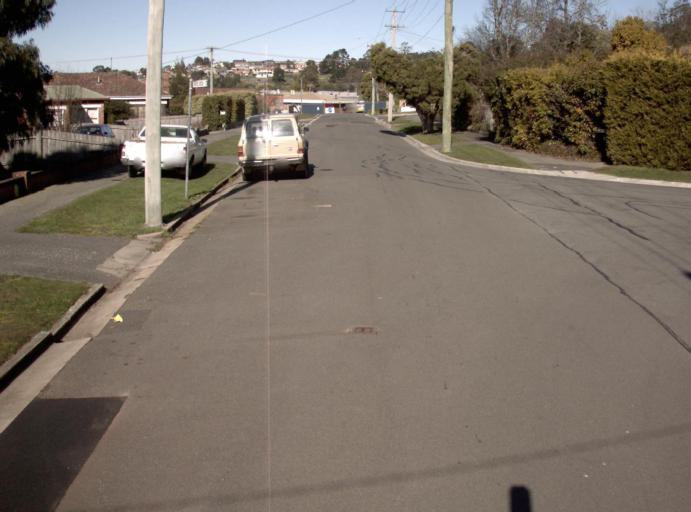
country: AU
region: Tasmania
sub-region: Launceston
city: Summerhill
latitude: -41.4718
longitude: 147.1574
